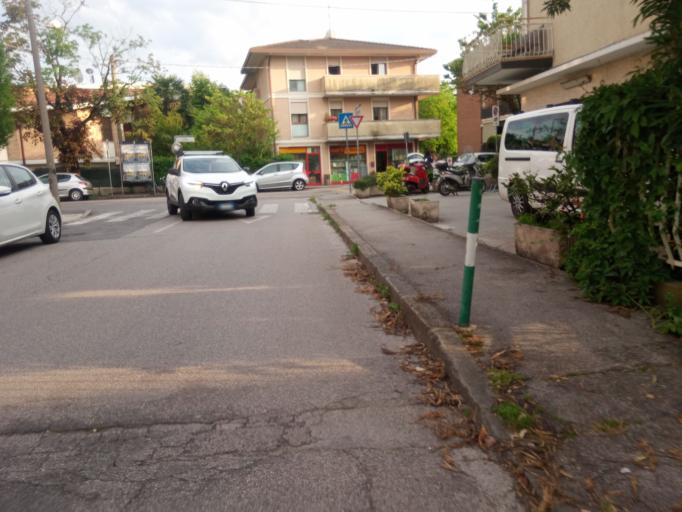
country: IT
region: Veneto
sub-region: Provincia di Padova
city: Mandriola-Sant'Agostino
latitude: 45.3834
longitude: 11.8517
